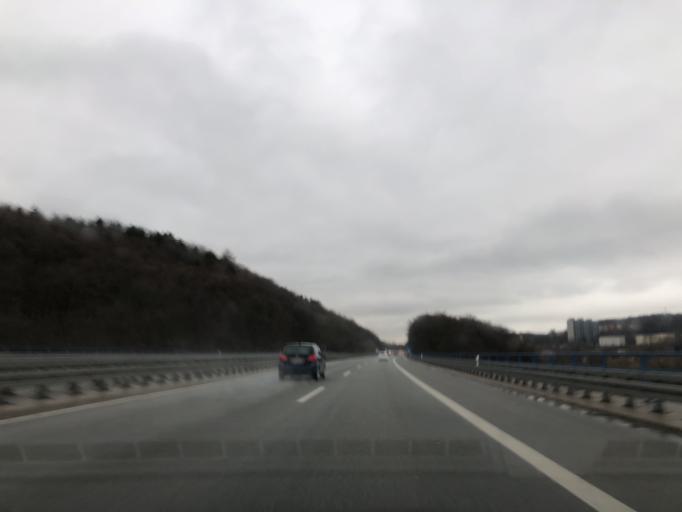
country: DE
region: North Rhine-Westphalia
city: Iserlohn
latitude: 51.3885
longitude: 7.7130
